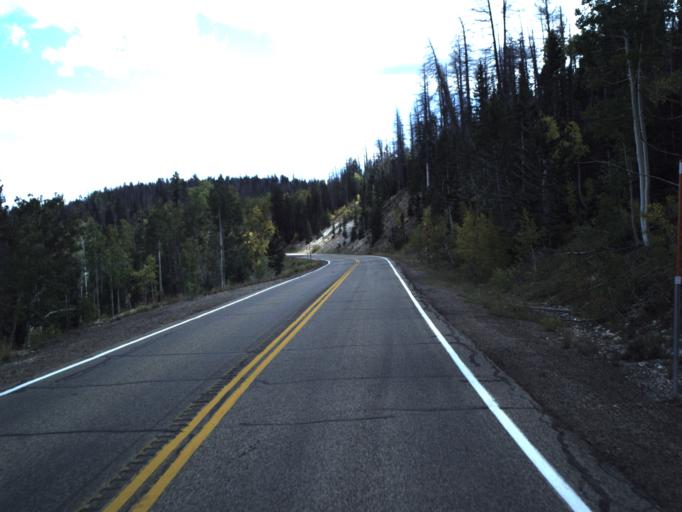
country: US
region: Utah
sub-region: Iron County
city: Parowan
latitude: 37.5377
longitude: -112.7744
